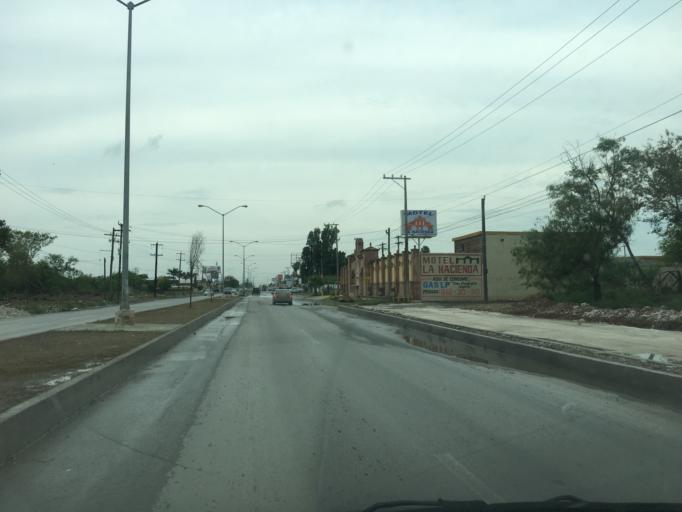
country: MX
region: Tamaulipas
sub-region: Matamoros
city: Heroica Matamoros
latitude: 25.8716
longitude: -97.5444
